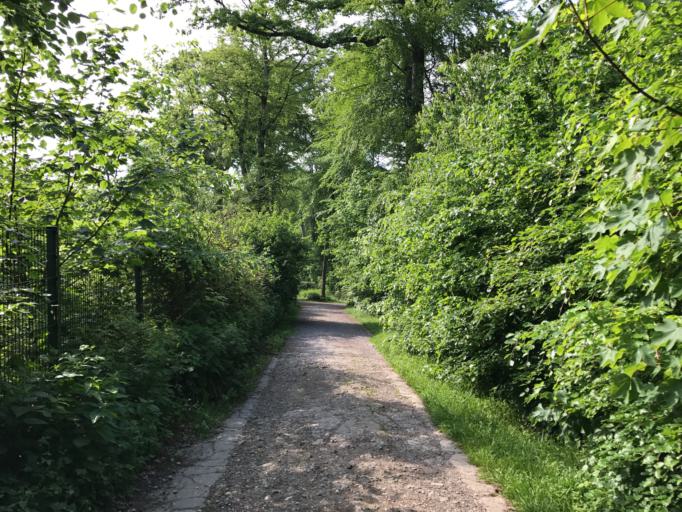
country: DE
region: North Rhine-Westphalia
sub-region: Regierungsbezirk Dusseldorf
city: Essen
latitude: 51.4163
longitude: 7.0374
